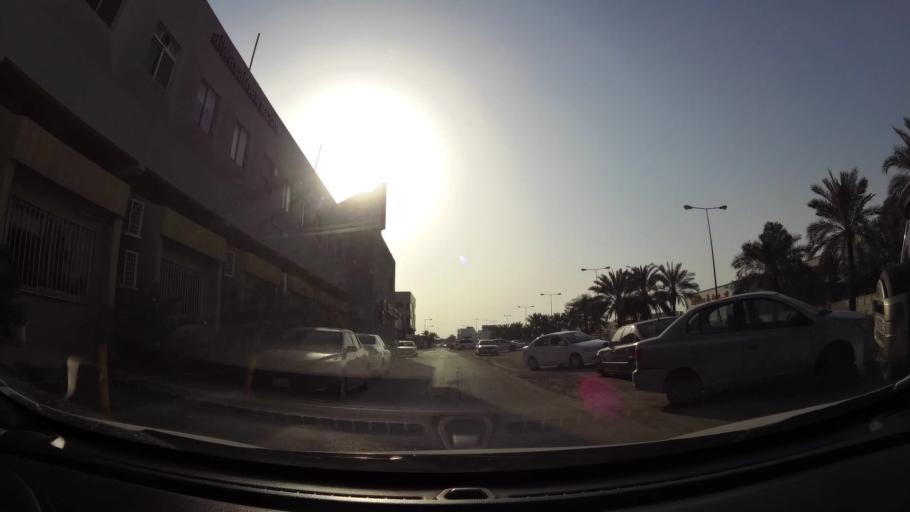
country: BH
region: Manama
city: Jidd Hafs
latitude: 26.2205
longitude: 50.5019
